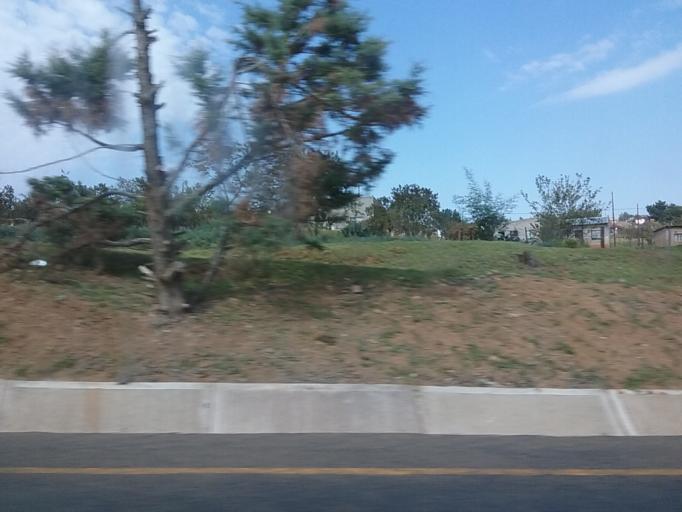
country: LS
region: Berea
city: Teyateyaneng
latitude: -29.1219
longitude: 27.9774
